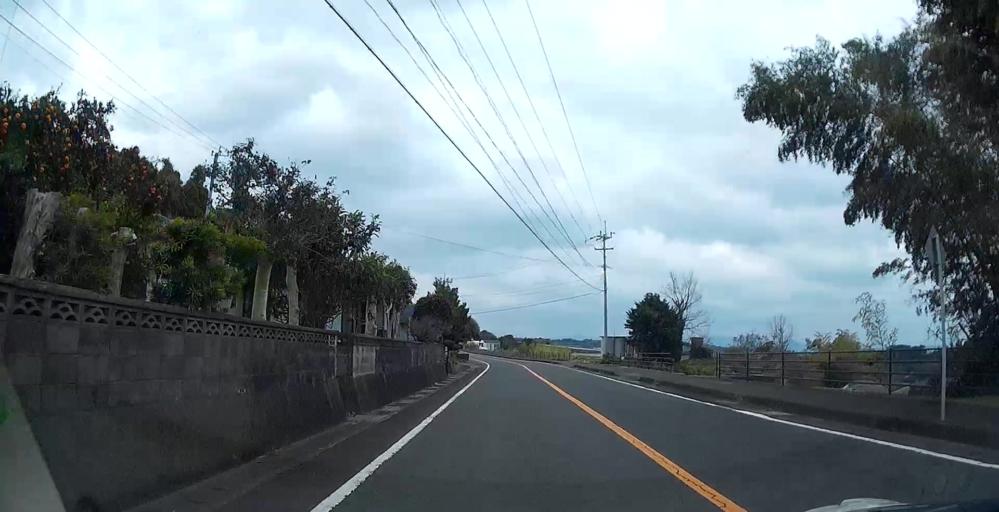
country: JP
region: Kagoshima
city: Akune
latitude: 32.0971
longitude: 130.1621
